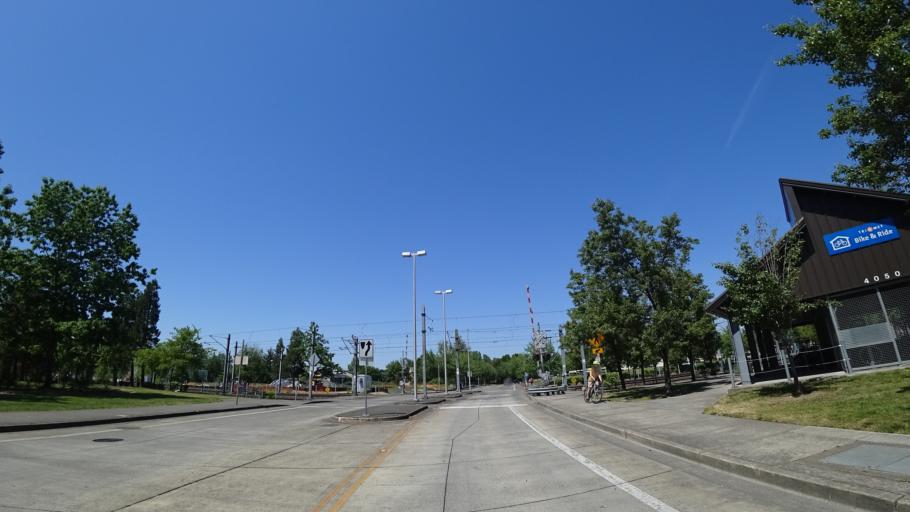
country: US
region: Oregon
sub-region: Washington County
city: Beaverton
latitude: 45.4906
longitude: -122.8021
